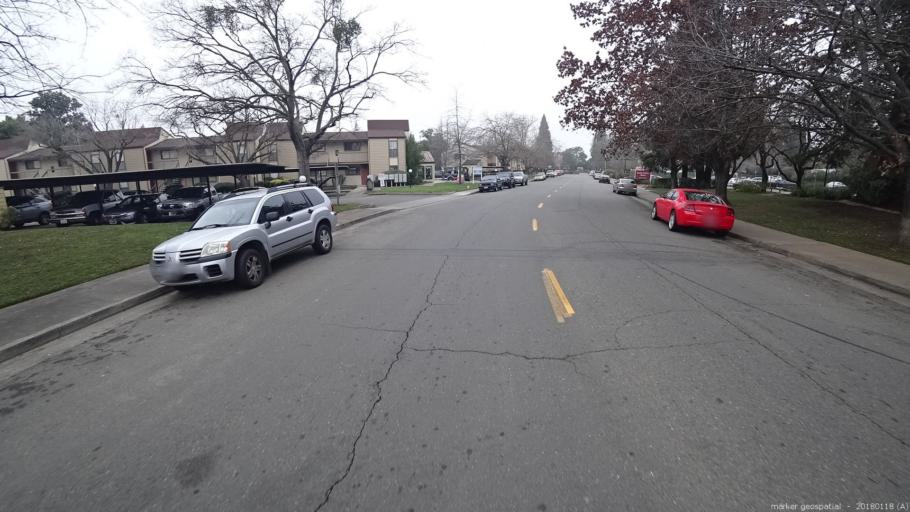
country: US
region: California
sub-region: Sacramento County
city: La Riviera
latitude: 38.5764
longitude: -121.3298
